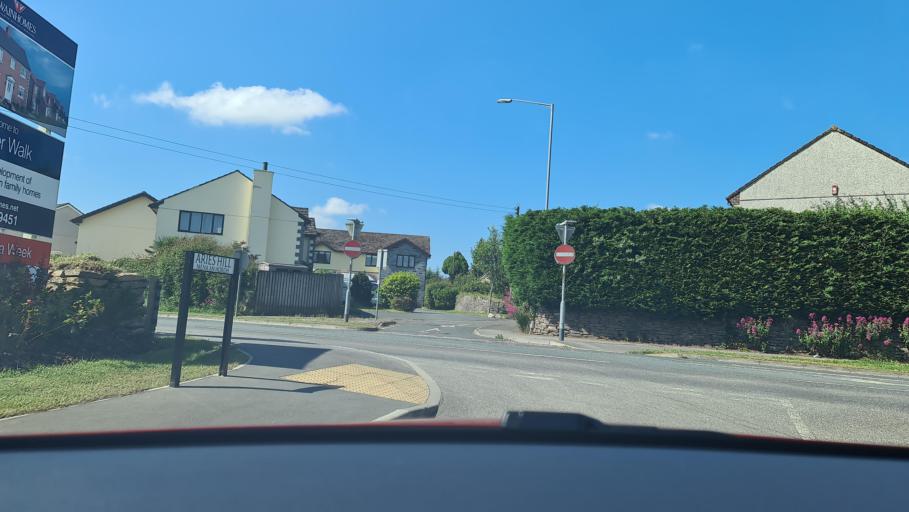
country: GB
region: England
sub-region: Cornwall
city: Liskeard
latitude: 50.4595
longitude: -4.4506
